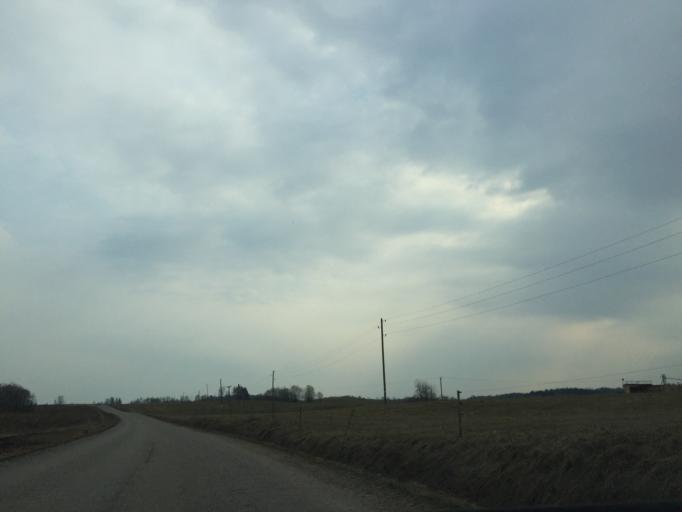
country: LV
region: Priekuli
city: Priekuli
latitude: 57.2441
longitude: 25.3728
